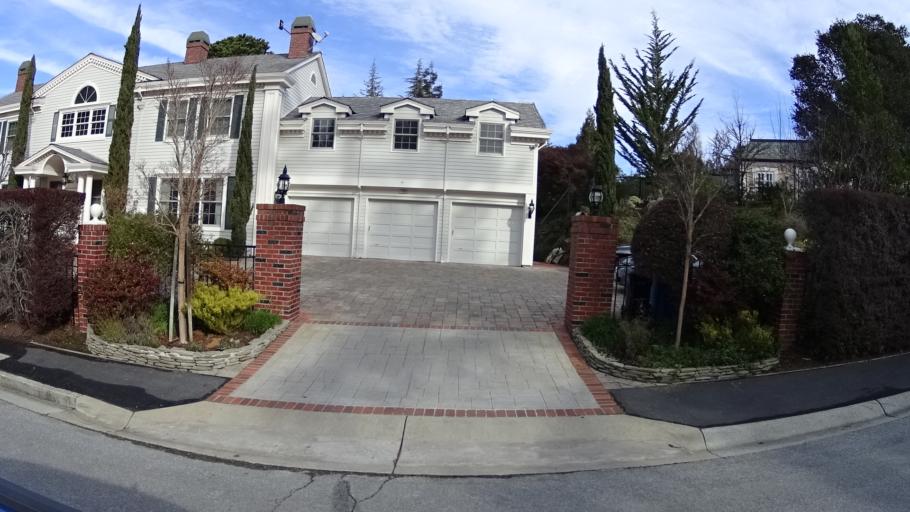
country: US
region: California
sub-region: San Mateo County
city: Hillsborough
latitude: 37.5611
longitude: -122.3617
